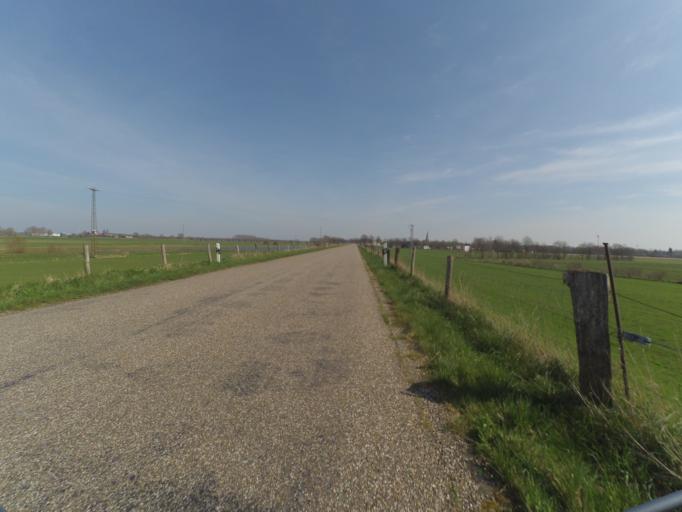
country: DE
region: North Rhine-Westphalia
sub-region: Regierungsbezirk Dusseldorf
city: Kleve
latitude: 51.8254
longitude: 6.1559
